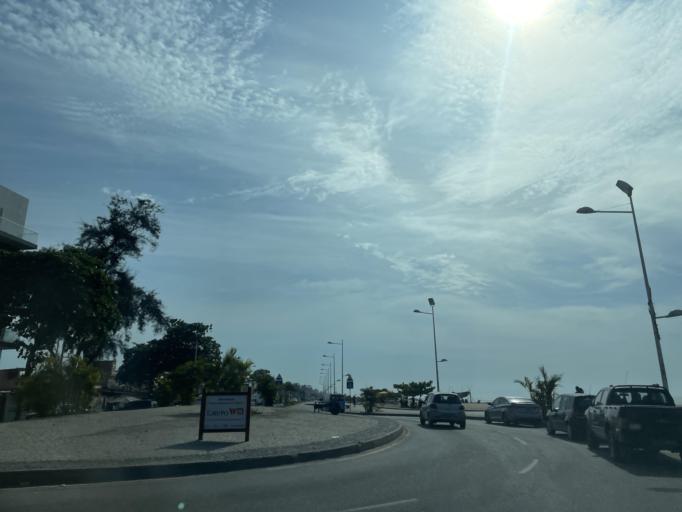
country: AO
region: Luanda
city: Luanda
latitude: -8.7704
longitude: 13.2521
